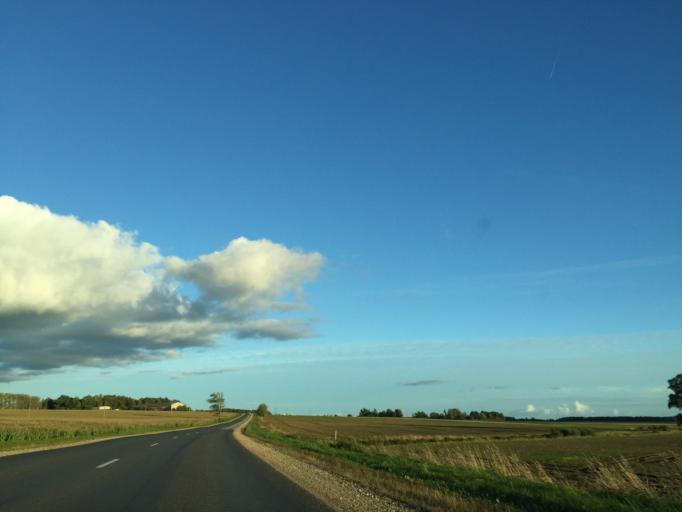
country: LV
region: Saldus Rajons
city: Saldus
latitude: 56.7109
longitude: 22.4142
